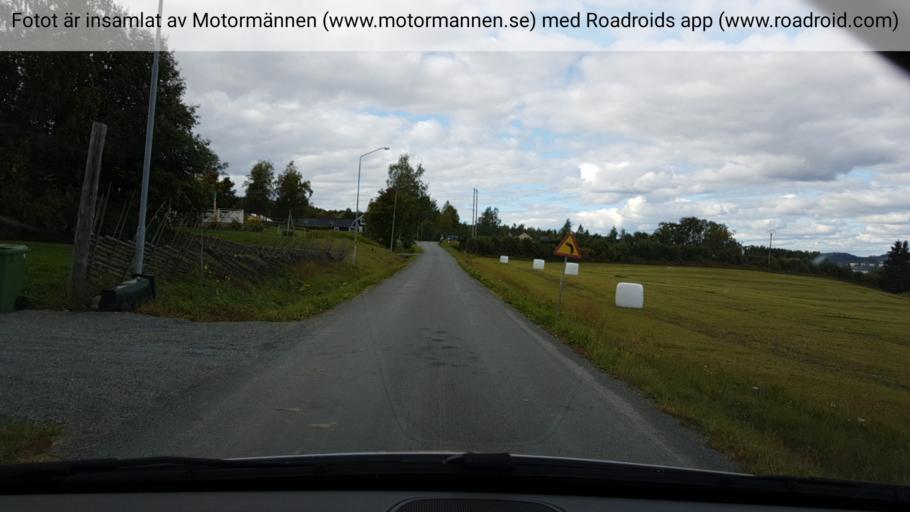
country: SE
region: Jaemtland
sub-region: OEstersunds Kommun
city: Ostersund
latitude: 63.1299
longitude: 14.6440
